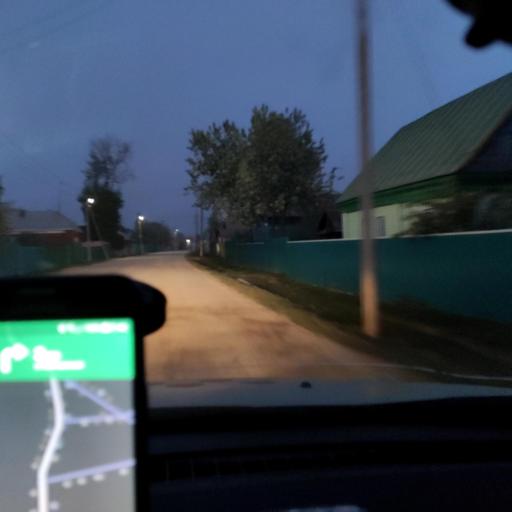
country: RU
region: Bashkortostan
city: Kabakovo
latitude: 54.6742
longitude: 56.2763
